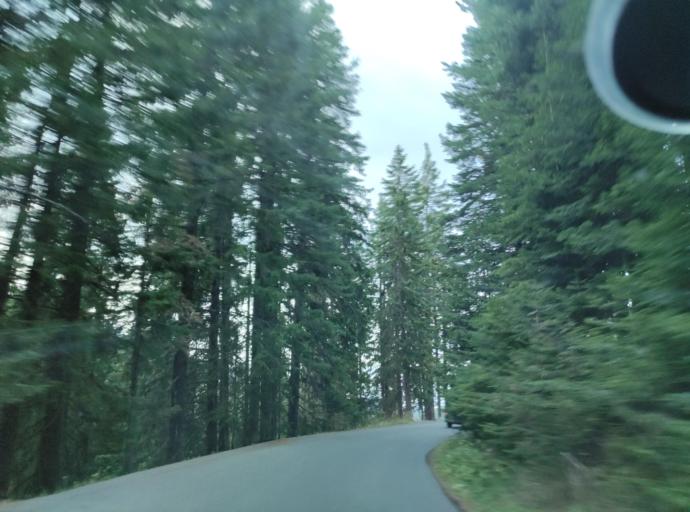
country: BG
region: Blagoevgrad
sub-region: Obshtina Bansko
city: Bansko
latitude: 41.7757
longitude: 23.4373
